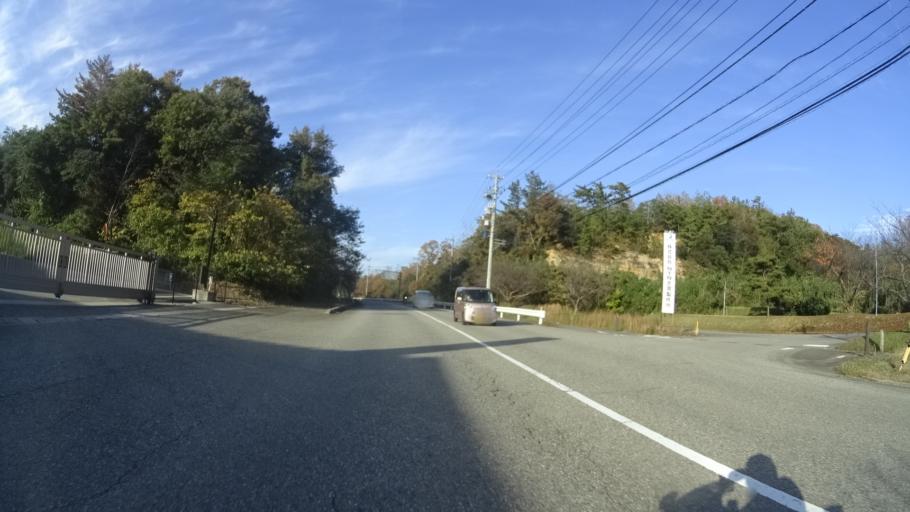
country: JP
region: Ishikawa
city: Hakui
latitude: 37.0372
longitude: 136.7787
